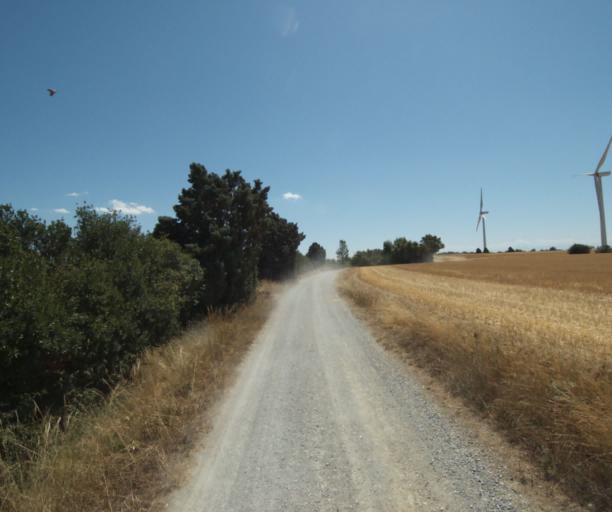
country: FR
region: Midi-Pyrenees
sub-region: Departement de la Haute-Garonne
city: Saint-Felix-Lauragais
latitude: 43.4672
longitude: 1.9208
